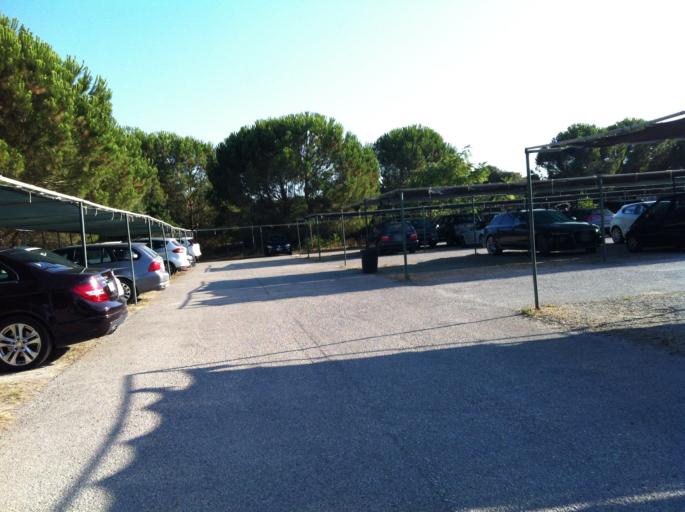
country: IT
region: Latium
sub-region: Provincia di Viterbo
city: Pescia Romana
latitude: 42.3808
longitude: 11.4465
